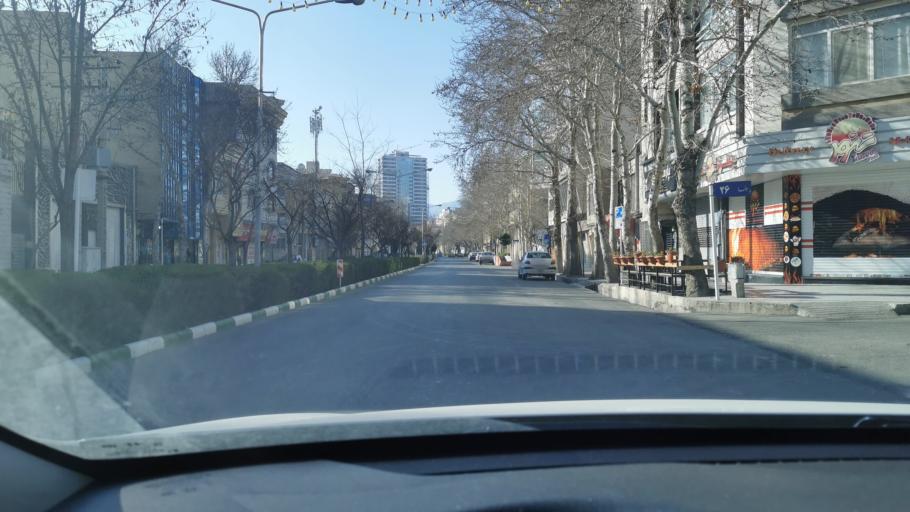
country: IR
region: Razavi Khorasan
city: Mashhad
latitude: 36.2900
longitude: 59.5673
